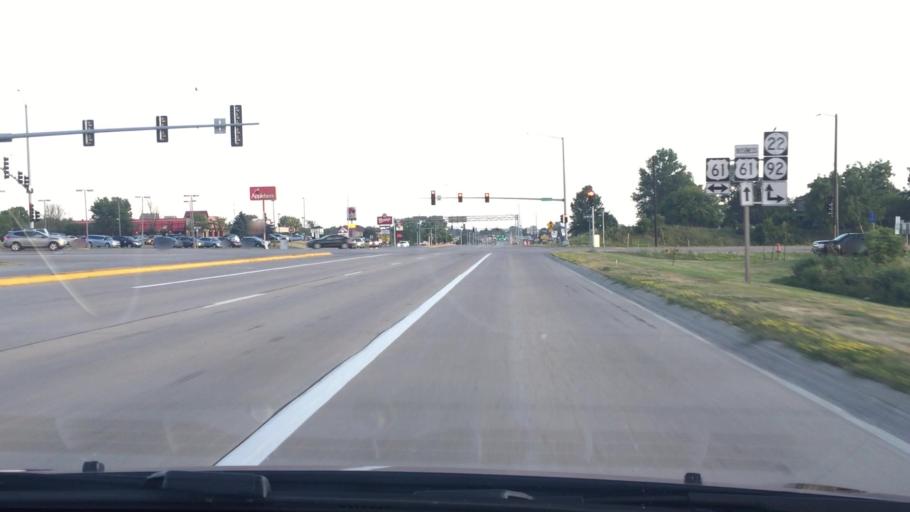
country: US
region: Iowa
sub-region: Muscatine County
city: Muscatine
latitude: 41.4544
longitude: -91.0303
